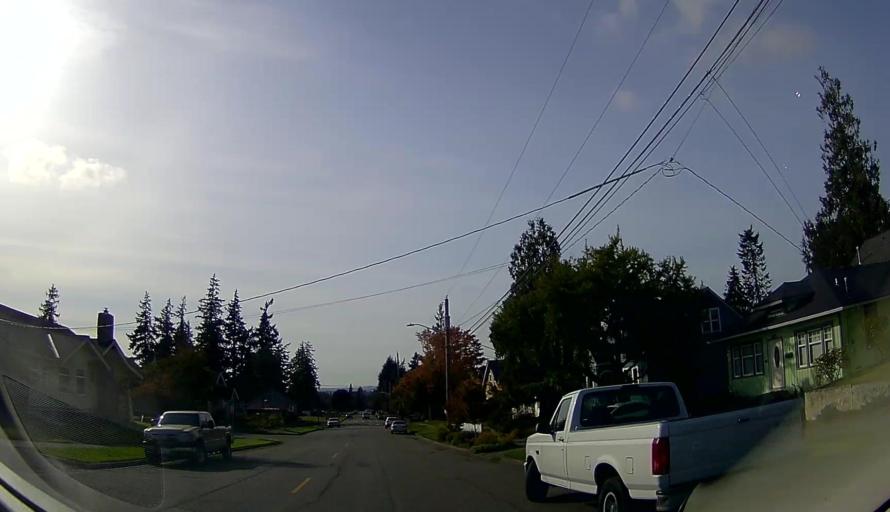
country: US
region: Washington
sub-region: Skagit County
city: Mount Vernon
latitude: 48.4243
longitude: -122.3311
